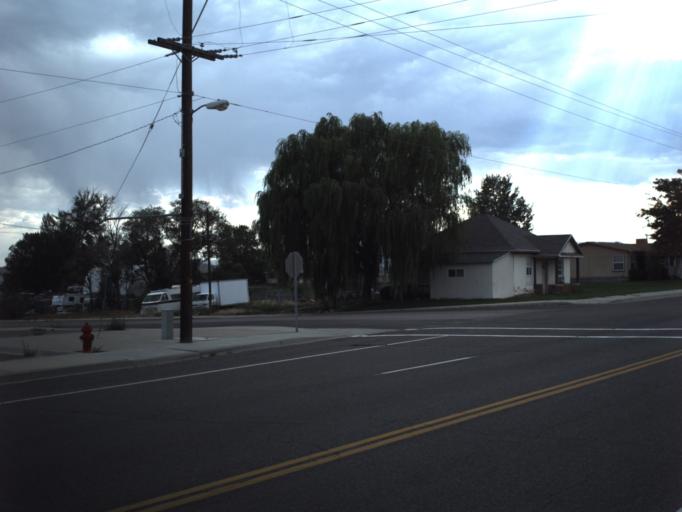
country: US
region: Utah
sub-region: Emery County
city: Huntington
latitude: 39.3487
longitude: -110.8576
